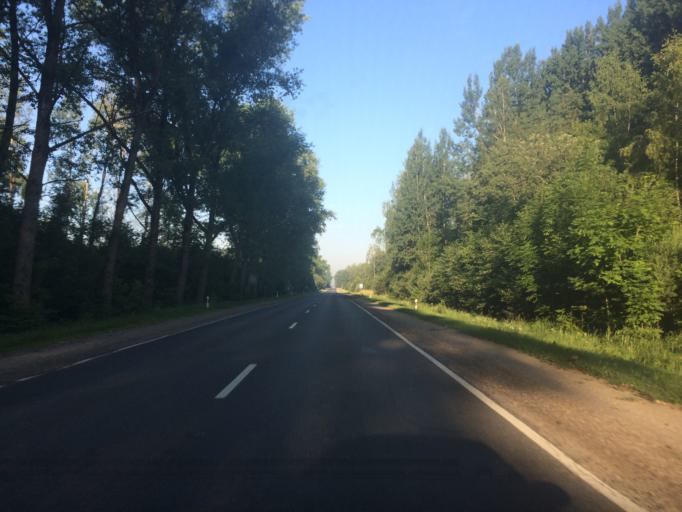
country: LT
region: Utenos apskritis
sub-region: Anyksciai
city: Anyksciai
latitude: 55.3573
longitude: 24.9706
